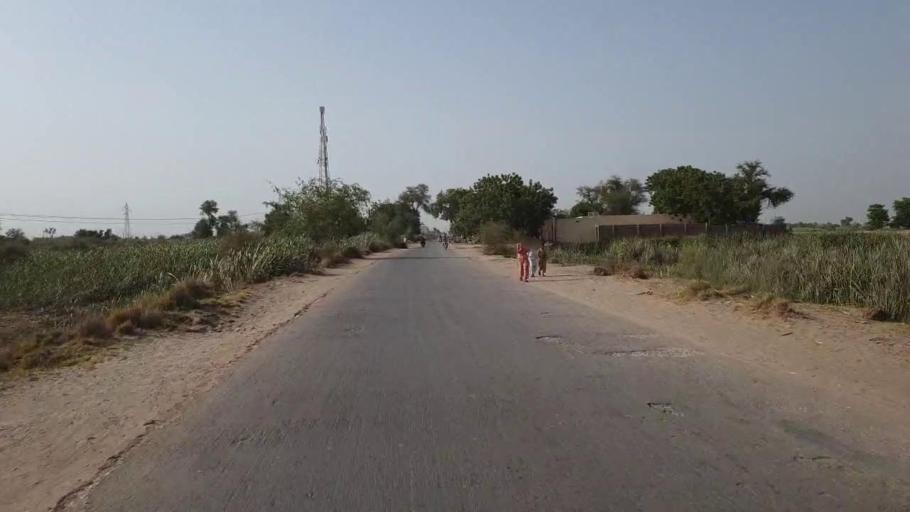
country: PK
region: Sindh
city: Sanghar
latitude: 26.2656
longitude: 68.9294
